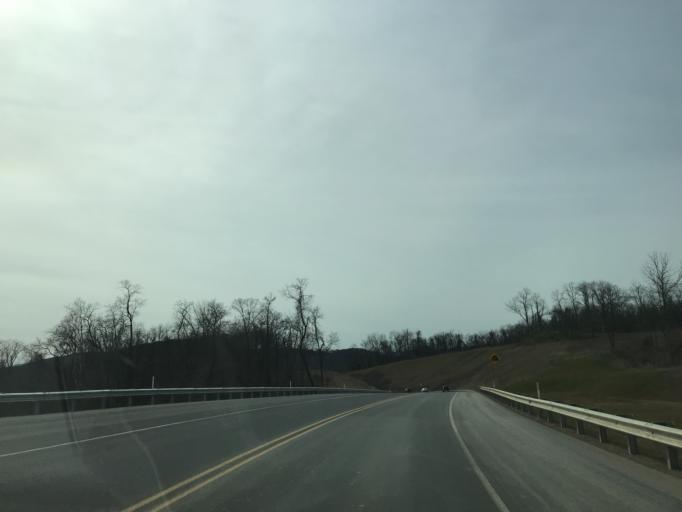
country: US
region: Pennsylvania
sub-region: Northumberland County
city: Northumberland
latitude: 40.9178
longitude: -76.8372
